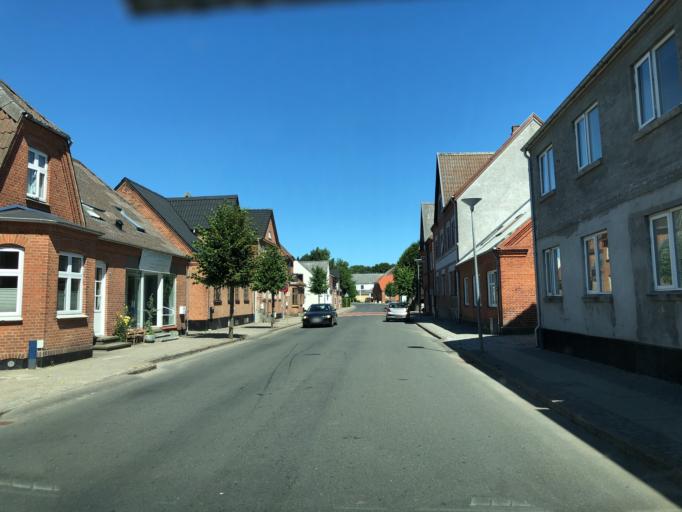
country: DK
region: Central Jutland
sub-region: Viborg Kommune
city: Viborg
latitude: 56.5572
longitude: 9.4036
